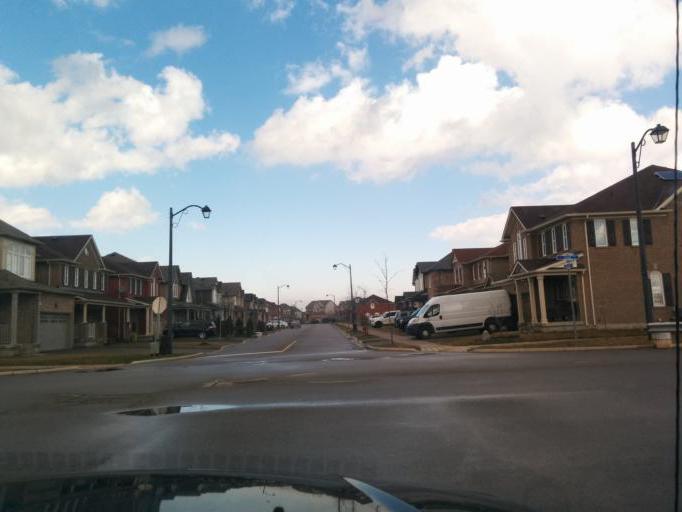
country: CA
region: Ontario
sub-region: Halton
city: Milton
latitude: 43.4804
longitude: -79.8713
